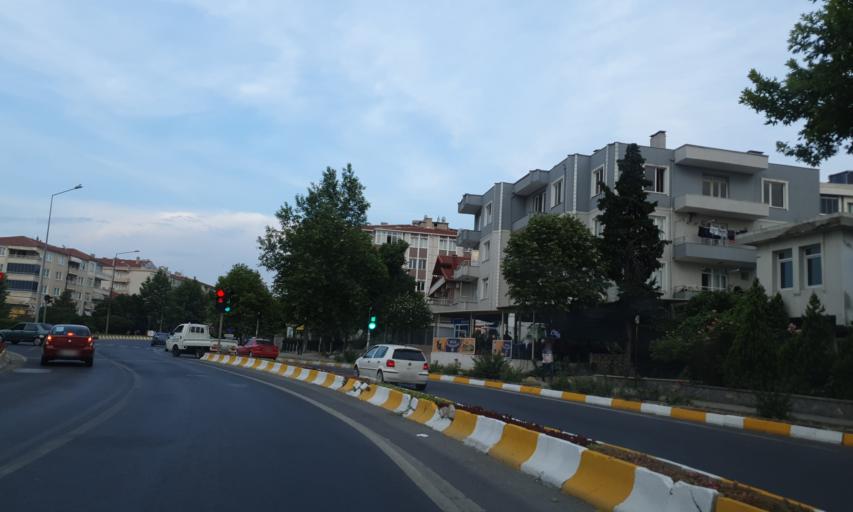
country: TR
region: Kirklareli
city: Luleburgaz
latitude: 41.4024
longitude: 27.3657
